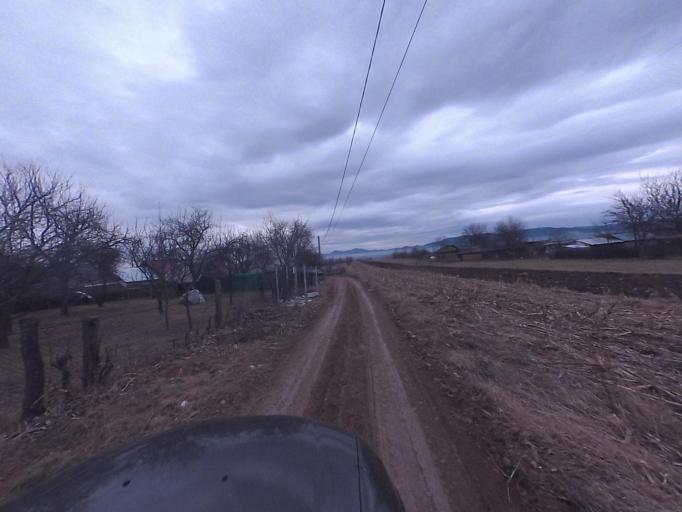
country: RO
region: Neamt
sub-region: Oras Targu Neamt
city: Humulesti
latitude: 47.1917
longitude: 26.3363
